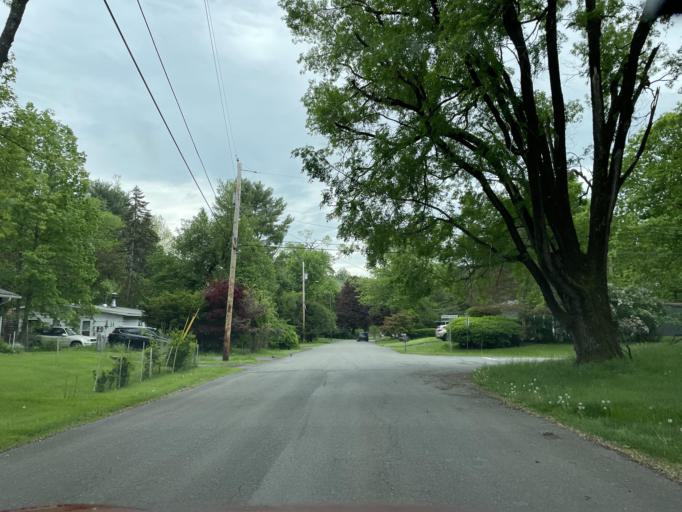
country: US
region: New York
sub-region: Ulster County
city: Woodstock
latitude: 42.0381
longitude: -74.1506
